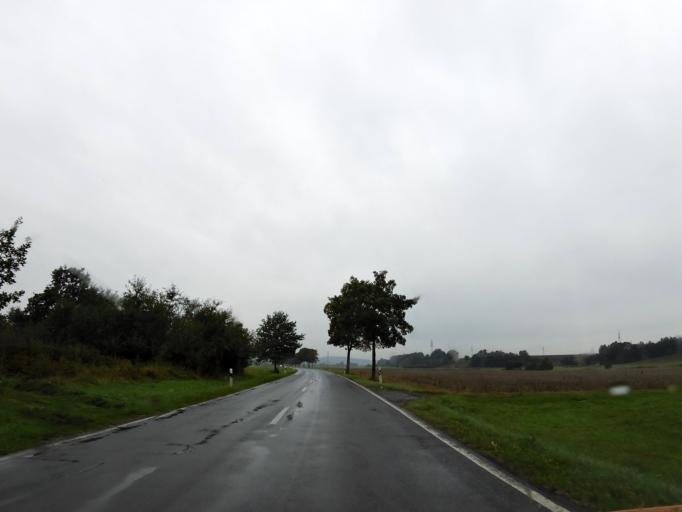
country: DE
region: Lower Saxony
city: Herzberg am Harz
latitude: 51.6302
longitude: 10.3377
